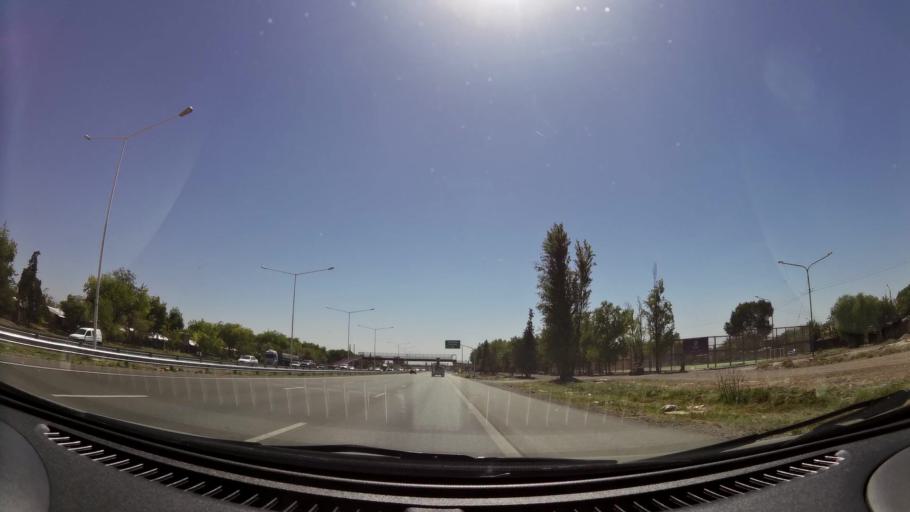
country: AR
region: Mendoza
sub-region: Departamento de Godoy Cruz
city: Godoy Cruz
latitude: -32.9582
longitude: -68.8367
